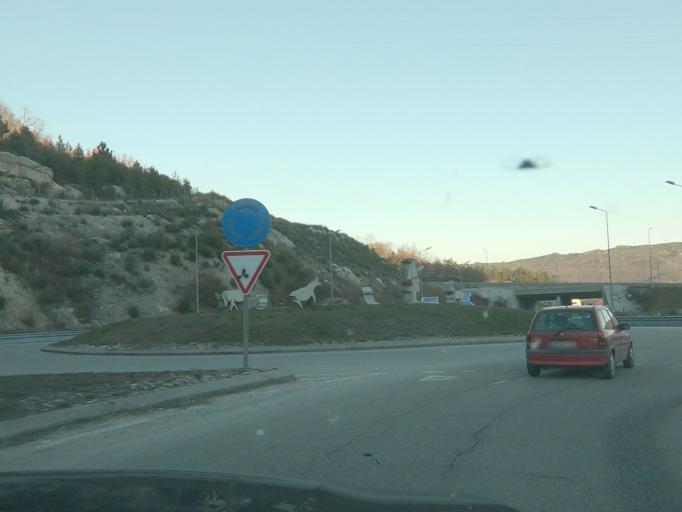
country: PT
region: Vila Real
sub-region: Vila Pouca de Aguiar
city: Vila Pouca de Aguiar
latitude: 41.4905
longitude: -7.6627
